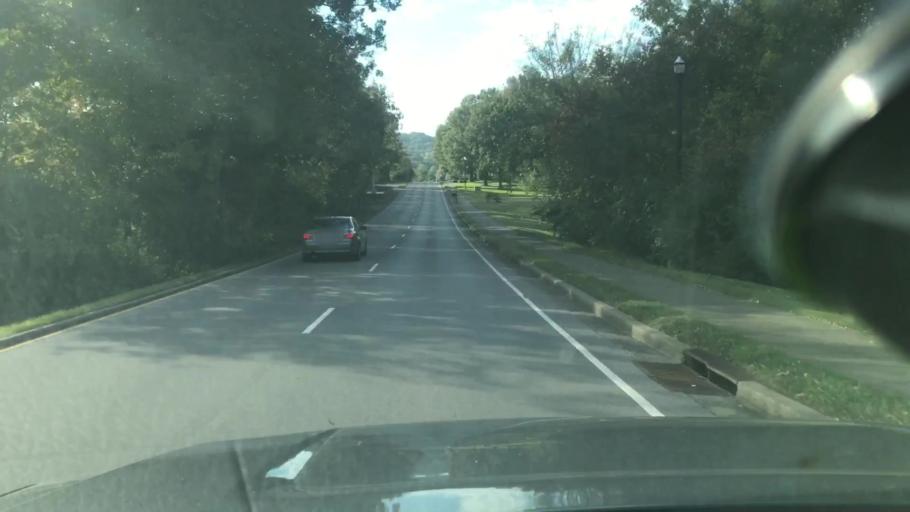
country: US
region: Tennessee
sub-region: Williamson County
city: Brentwood Estates
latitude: 36.0144
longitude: -86.8088
